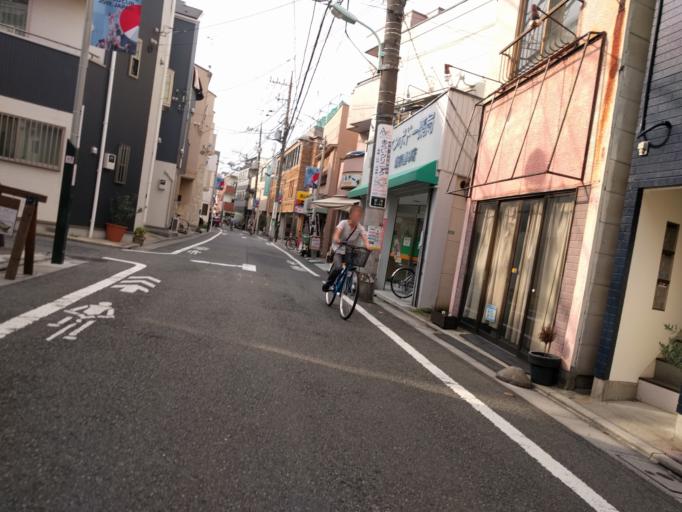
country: JP
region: Tokyo
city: Tokyo
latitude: 35.6544
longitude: 139.6330
